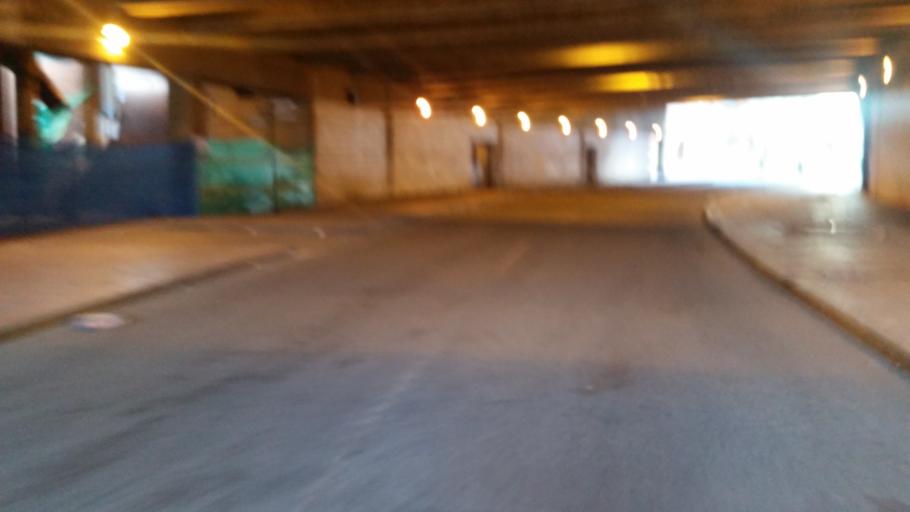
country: CO
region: Bogota D.C.
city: Bogota
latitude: 4.6176
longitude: -74.0703
